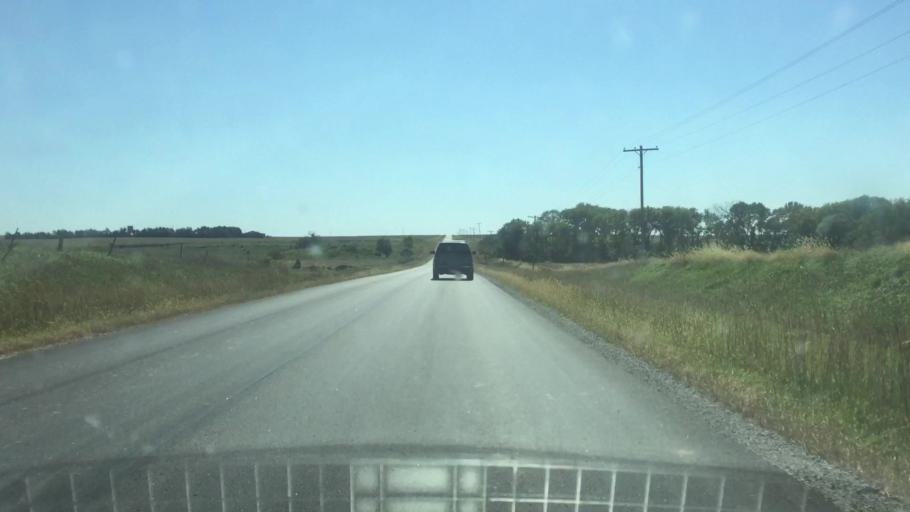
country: US
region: Kansas
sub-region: Marshall County
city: Marysville
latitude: 39.8789
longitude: -96.6010
